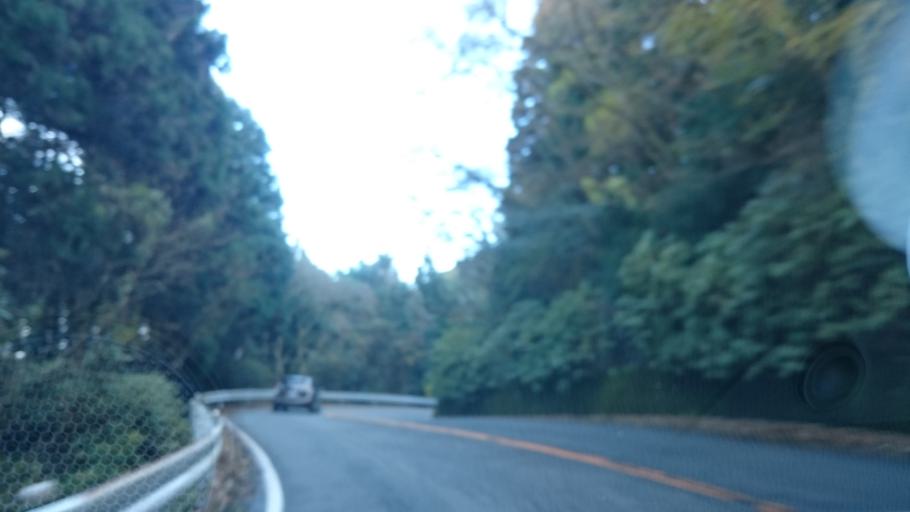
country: JP
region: Shizuoka
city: Heda
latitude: 34.9770
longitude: 138.8692
